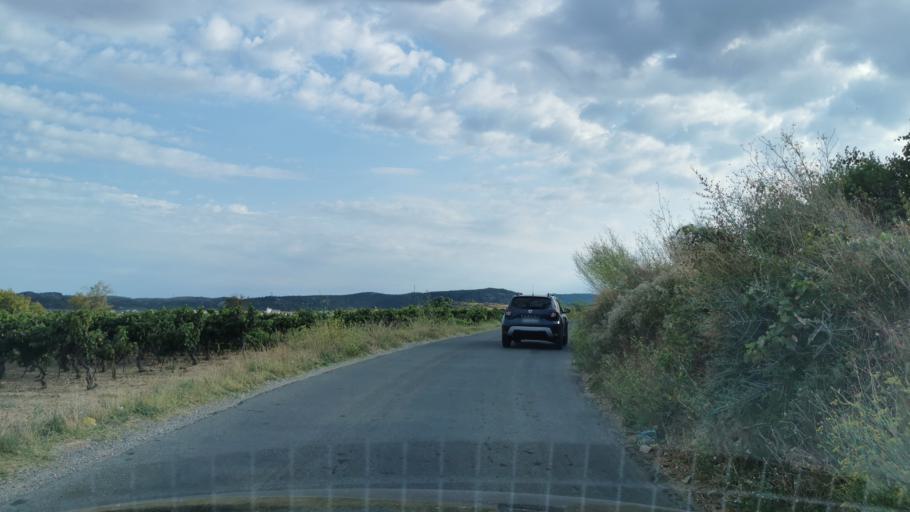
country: FR
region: Languedoc-Roussillon
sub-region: Departement de l'Aude
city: Marcorignan
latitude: 43.1984
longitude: 2.9319
